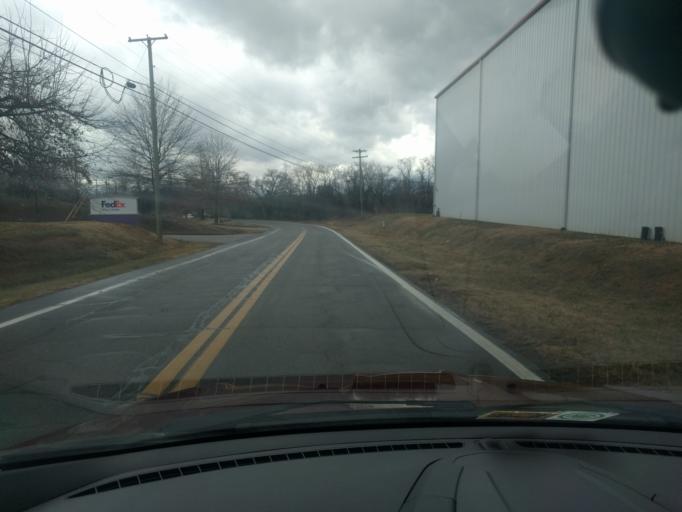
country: US
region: Virginia
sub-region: Roanoke County
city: Hollins
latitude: 37.3149
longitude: -79.9785
